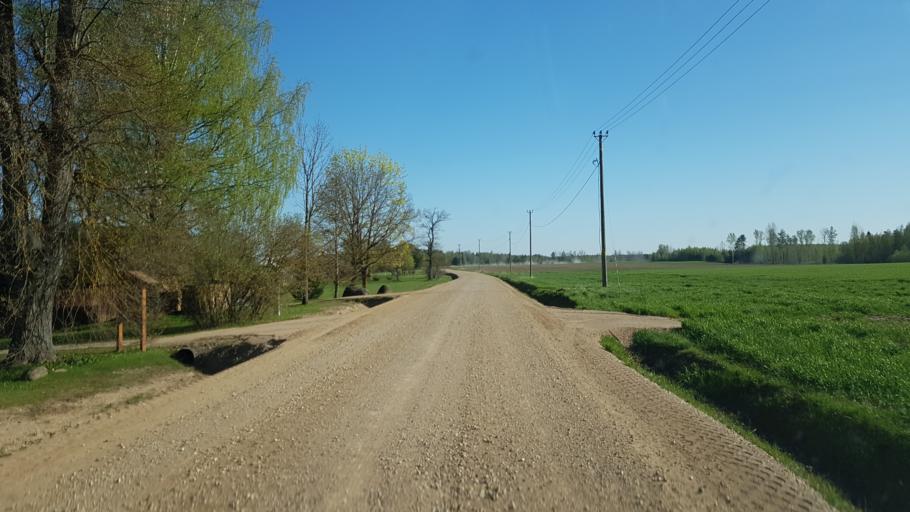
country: EE
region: Polvamaa
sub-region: Polva linn
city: Polva
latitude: 58.0972
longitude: 27.2221
